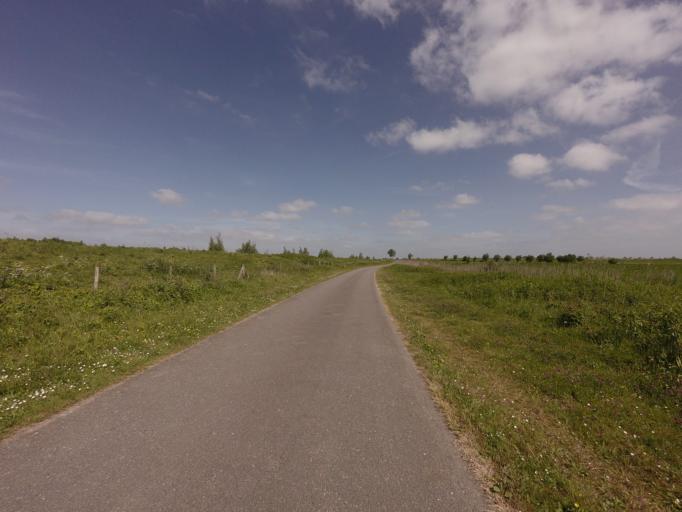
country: NL
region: North Brabant
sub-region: Gemeente Steenbergen
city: Dinteloord
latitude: 51.7345
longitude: 4.3440
